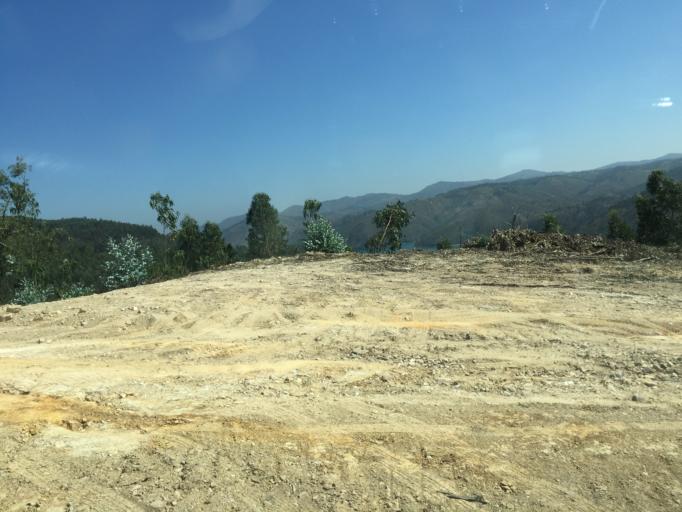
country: PT
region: Santarem
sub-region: Ferreira do Zezere
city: Ferreira do Zezere
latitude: 39.6546
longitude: -8.2387
